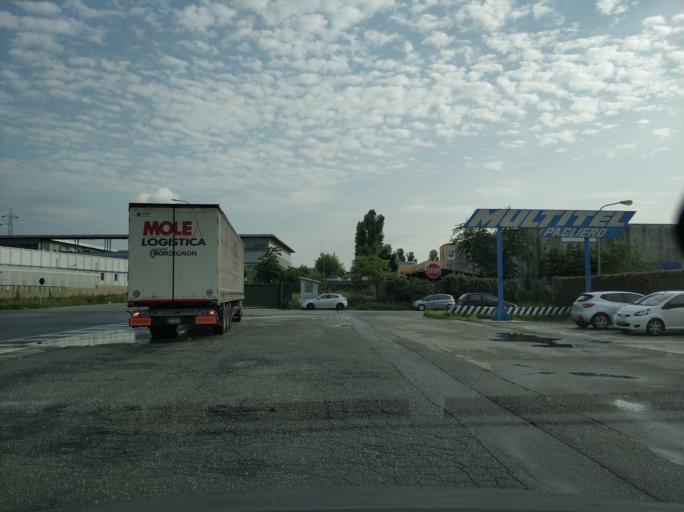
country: IT
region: Piedmont
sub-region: Provincia di Torino
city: Settimo Torinese
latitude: 45.1206
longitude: 7.7508
